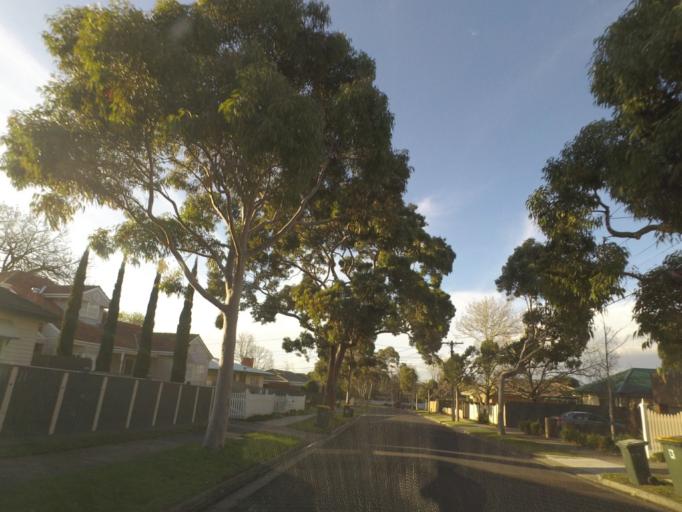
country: AU
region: Victoria
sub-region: Whitehorse
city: Blackburn North
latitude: -37.8093
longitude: 145.1545
